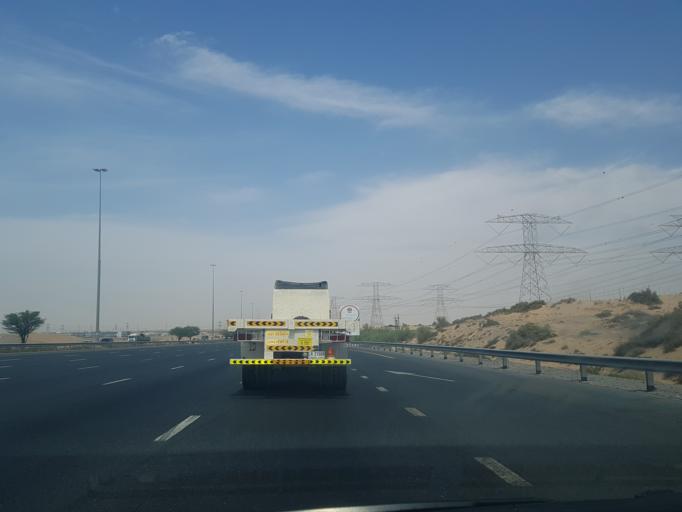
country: AE
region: Ash Shariqah
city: Sharjah
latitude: 25.2129
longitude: 55.5540
